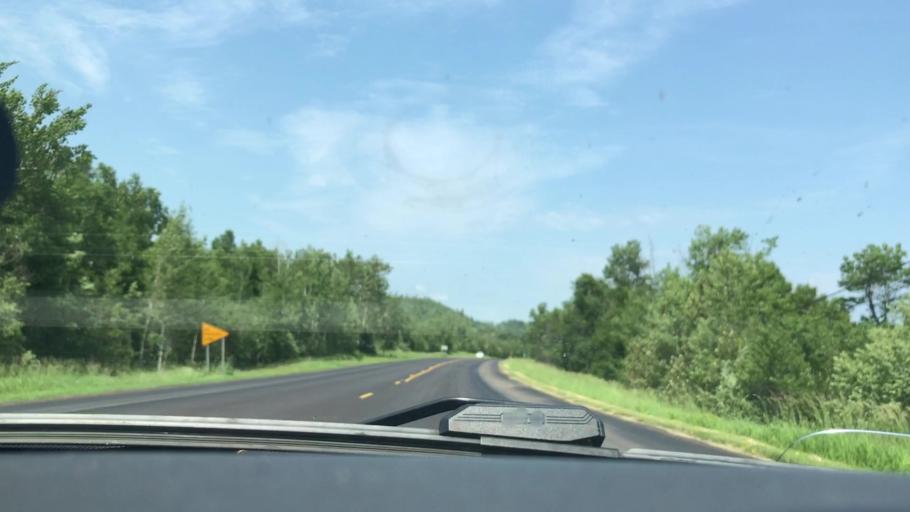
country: US
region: Minnesota
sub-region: Lake County
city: Silver Bay
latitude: 47.3537
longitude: -91.1819
